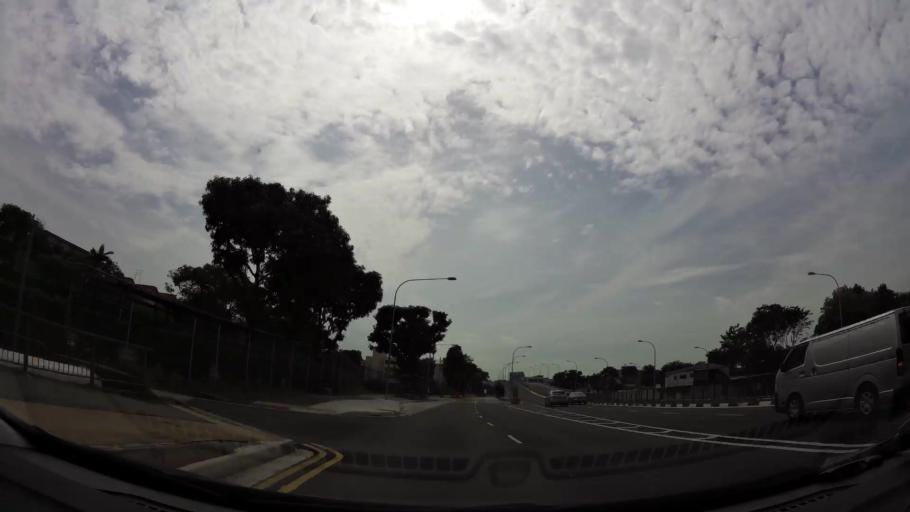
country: SG
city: Singapore
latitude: 1.3129
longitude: 103.7547
